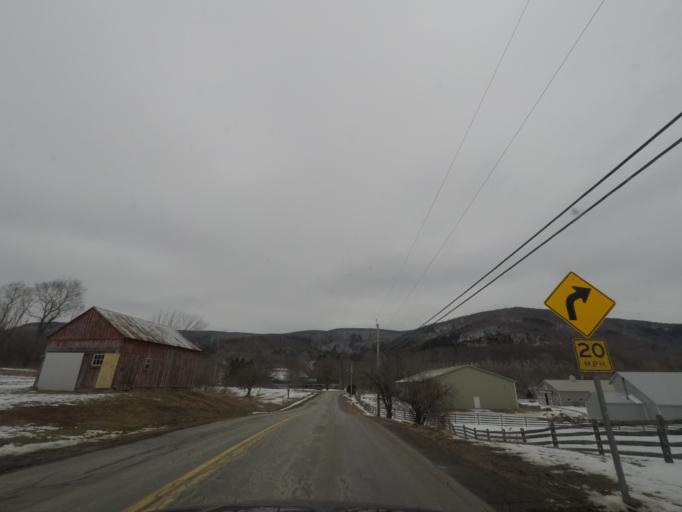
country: US
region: Massachusetts
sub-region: Berkshire County
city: Lanesborough
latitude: 42.5987
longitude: -73.3602
